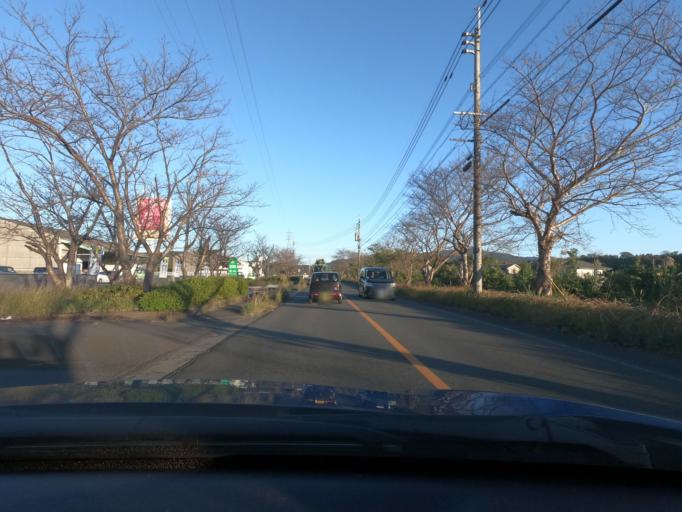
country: JP
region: Kagoshima
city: Satsumasendai
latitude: 31.8086
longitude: 130.3222
